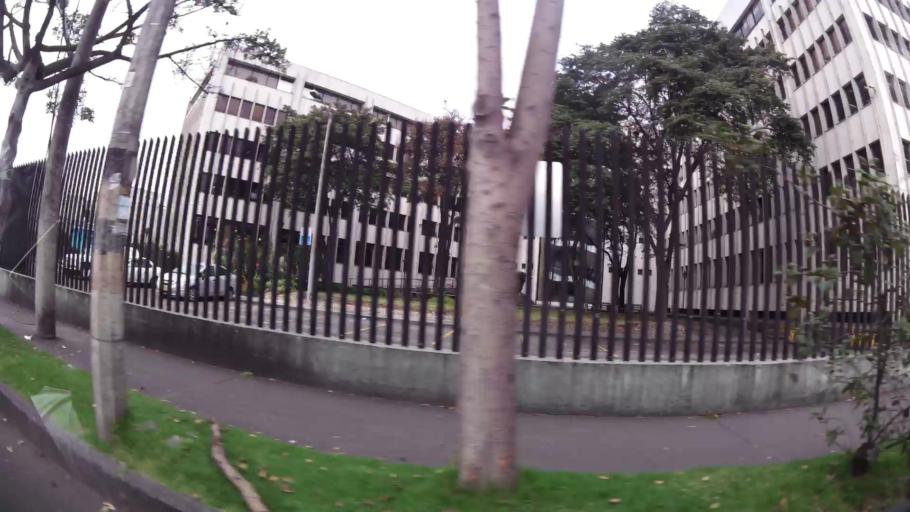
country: CO
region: Bogota D.C.
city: Barrio San Luis
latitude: 4.6852
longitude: -74.0728
